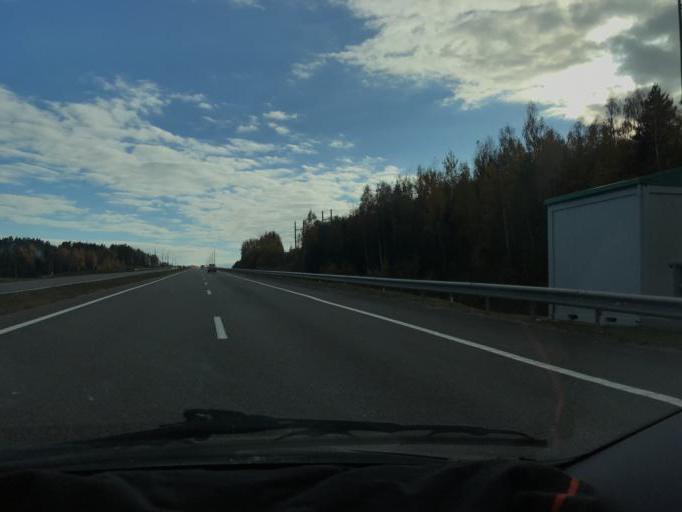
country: BY
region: Minsk
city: Lahoysk
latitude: 54.1843
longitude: 27.8171
